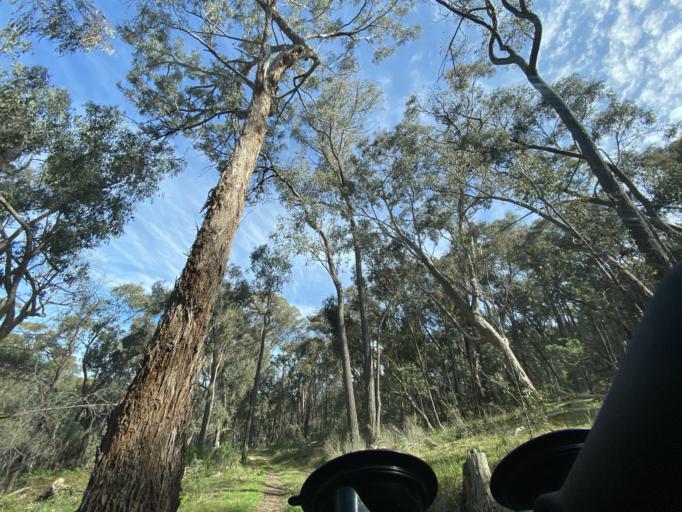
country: AU
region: Victoria
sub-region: Mansfield
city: Mansfield
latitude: -36.8097
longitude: 146.1160
